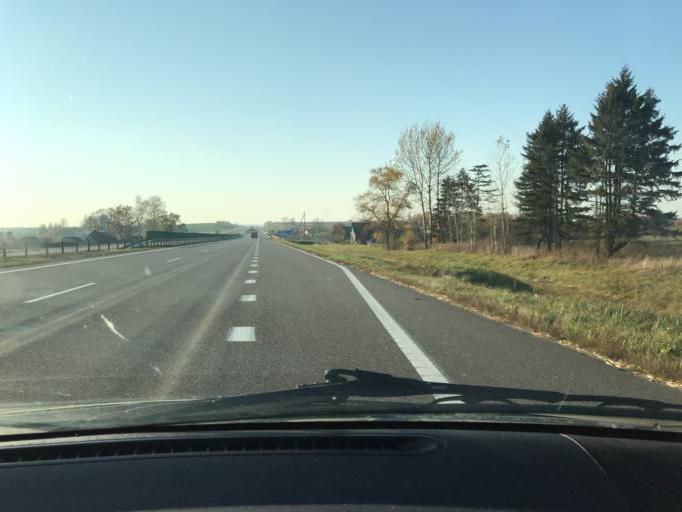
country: BY
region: Minsk
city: Loshnitsa
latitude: 54.2898
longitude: 28.8127
